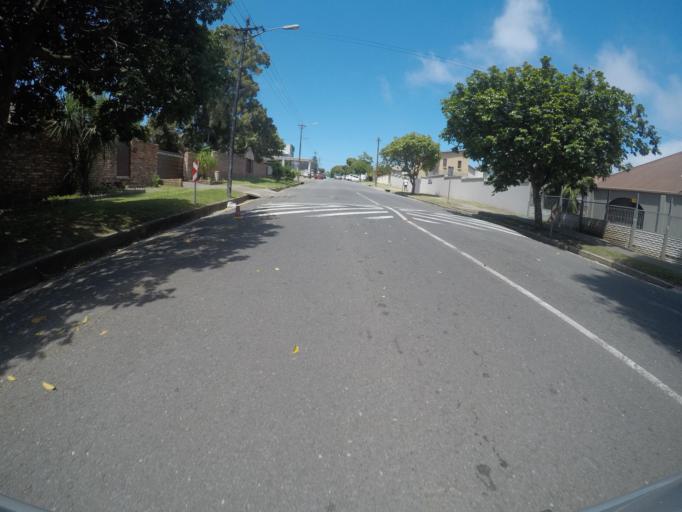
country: ZA
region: Eastern Cape
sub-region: Buffalo City Metropolitan Municipality
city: East London
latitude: -32.9896
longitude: 27.9057
